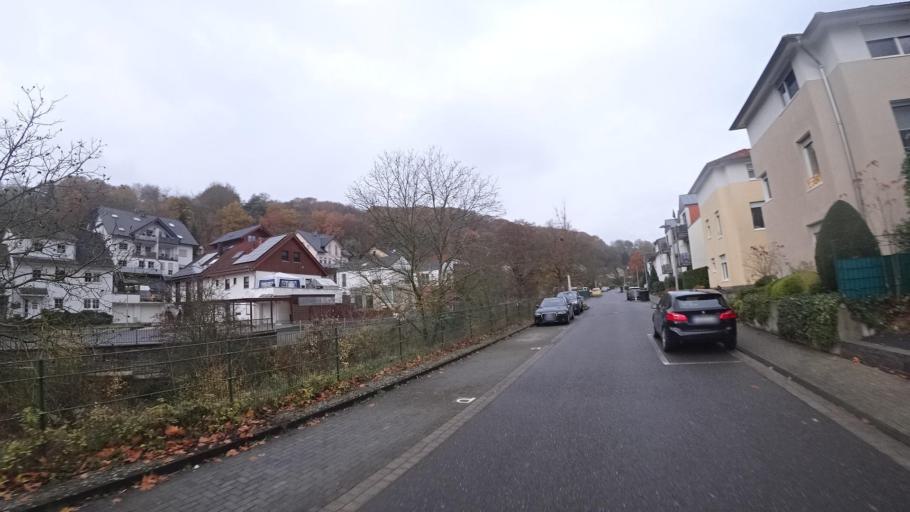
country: DE
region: Rheinland-Pfalz
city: Remagen
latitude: 50.5543
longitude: 7.1853
